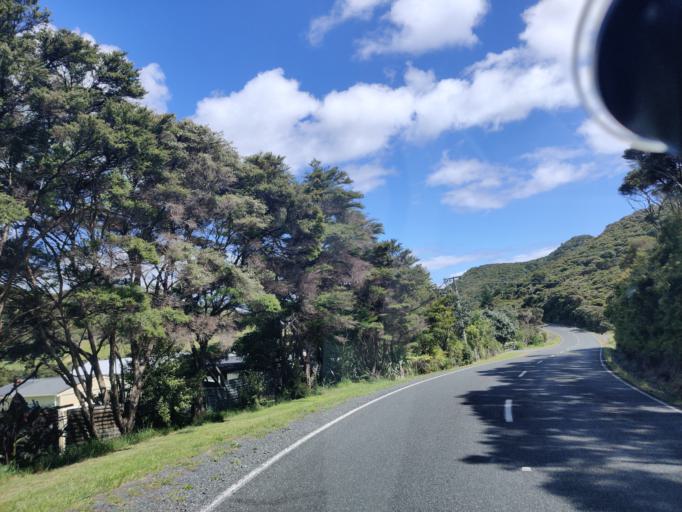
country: NZ
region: Northland
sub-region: Far North District
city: Paihia
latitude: -35.2673
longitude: 174.2715
